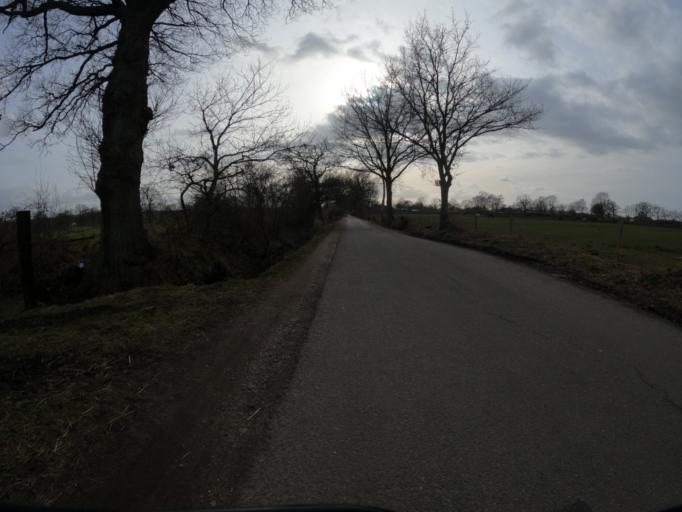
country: DE
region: Schleswig-Holstein
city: Rellingen
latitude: 53.5898
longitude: 9.8010
